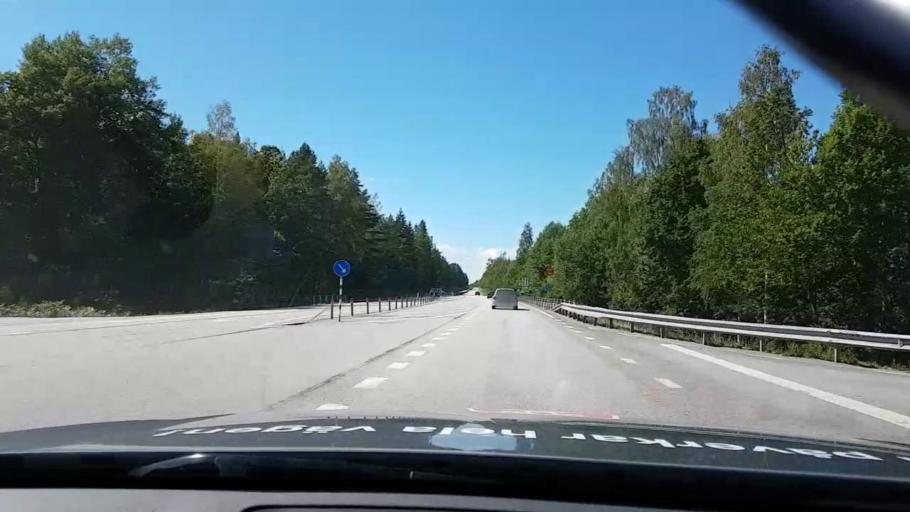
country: SE
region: Kalmar
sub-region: Vasterviks Kommun
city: Gamleby
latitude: 57.8178
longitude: 16.4774
